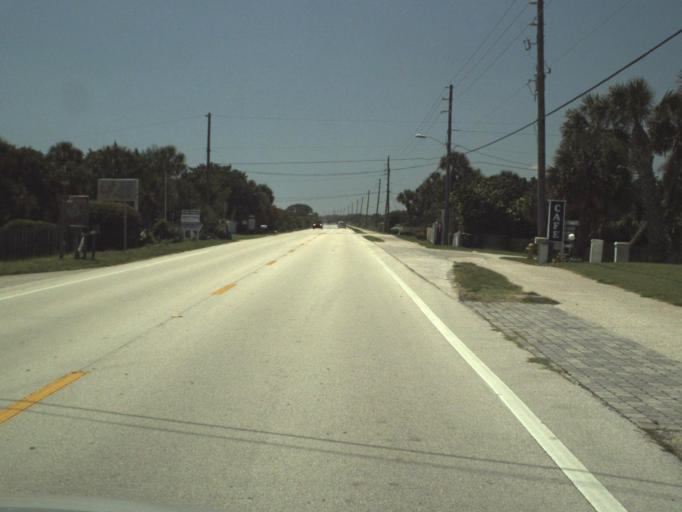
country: US
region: Florida
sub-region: Brevard County
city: Malabar
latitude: 28.0061
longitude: -80.5284
